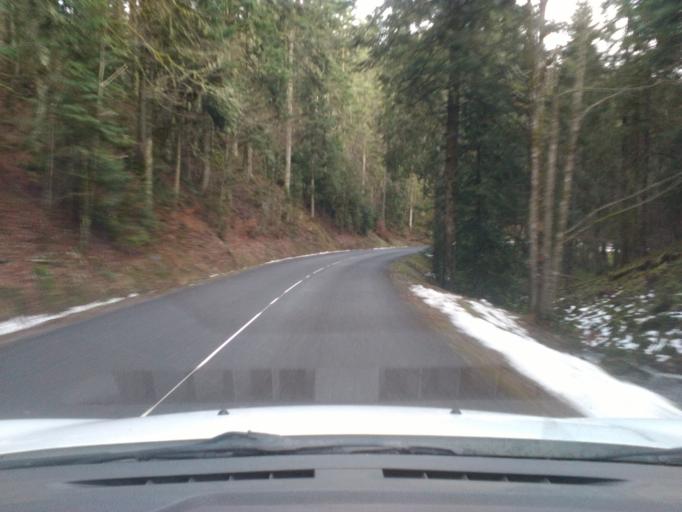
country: FR
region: Lorraine
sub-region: Departement des Vosges
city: Xonrupt-Longemer
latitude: 48.0974
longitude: 6.9697
